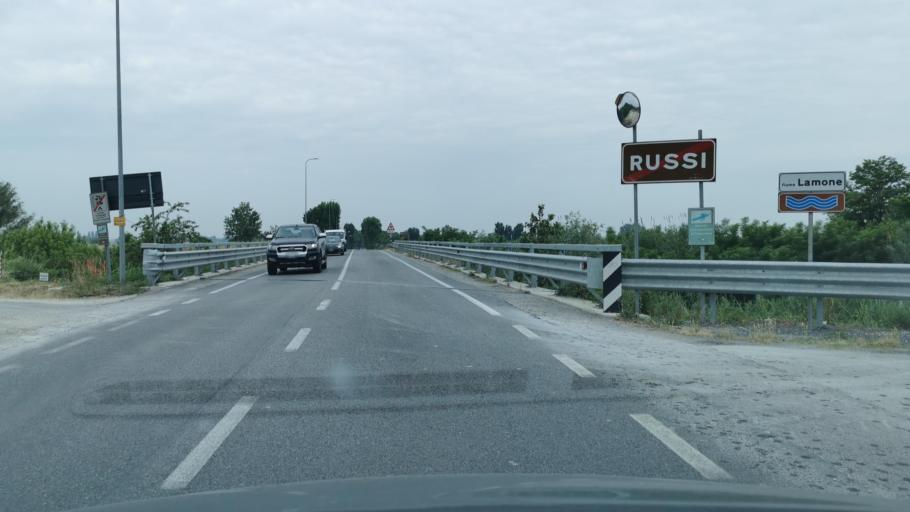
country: IT
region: Emilia-Romagna
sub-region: Provincia di Ravenna
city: Russi
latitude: 44.4013
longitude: 12.0245
